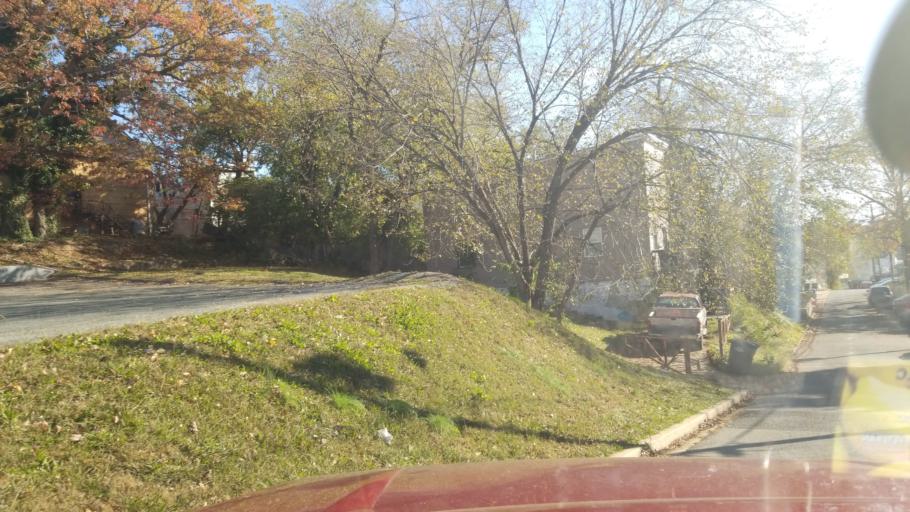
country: US
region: Maryland
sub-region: Prince George's County
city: Fairmount Heights
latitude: 38.9016
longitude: -76.9244
